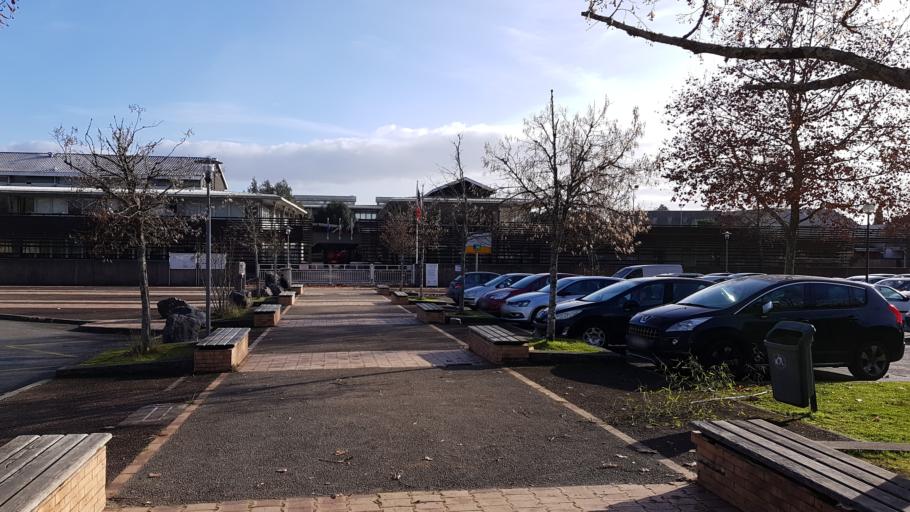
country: FR
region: Aquitaine
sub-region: Departement des Landes
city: Saint-Paul-les-Dax
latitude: 43.7269
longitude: -1.0432
